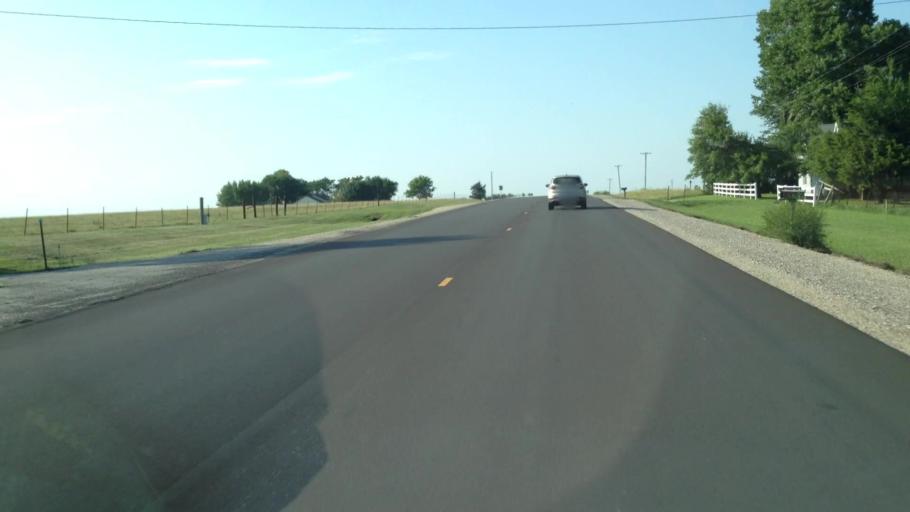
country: US
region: Kansas
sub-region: Anderson County
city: Garnett
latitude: 38.3501
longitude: -95.2488
